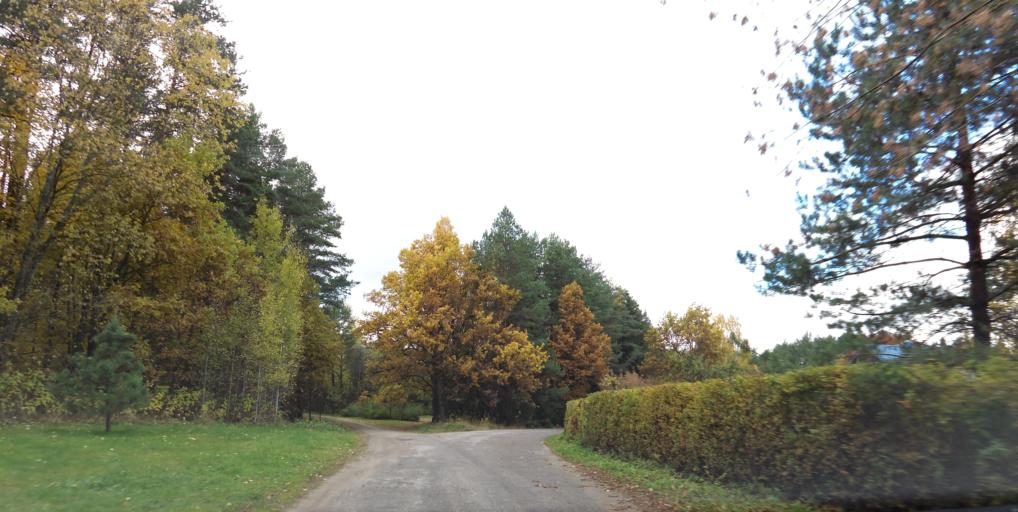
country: LT
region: Vilnius County
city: Vilkpede
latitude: 54.6476
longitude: 25.2551
